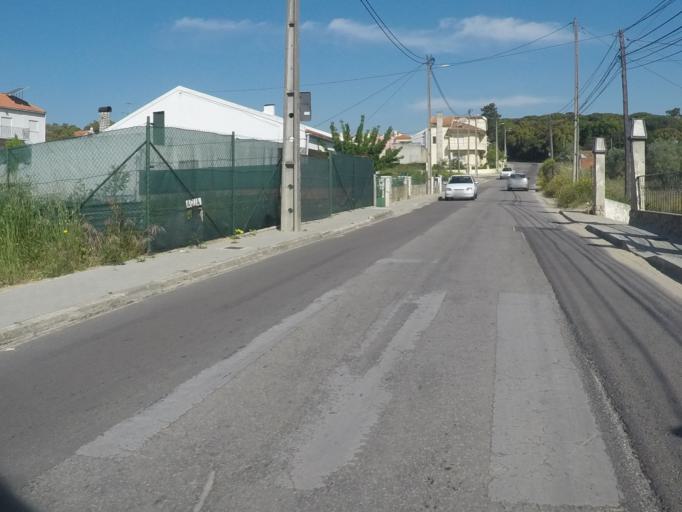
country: PT
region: Setubal
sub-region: Seixal
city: Amora
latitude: 38.6082
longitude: -9.1217
